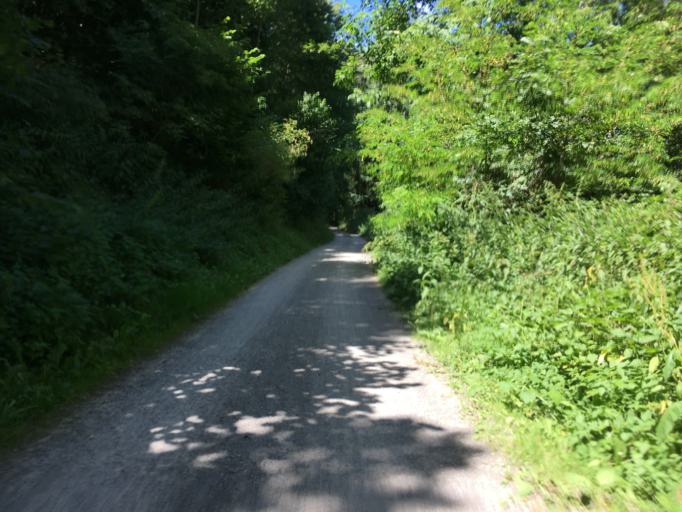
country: DE
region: Baden-Wuerttemberg
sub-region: Regierungsbezirk Stuttgart
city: Vaihingen an der Enz
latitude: 48.9158
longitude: 8.9586
